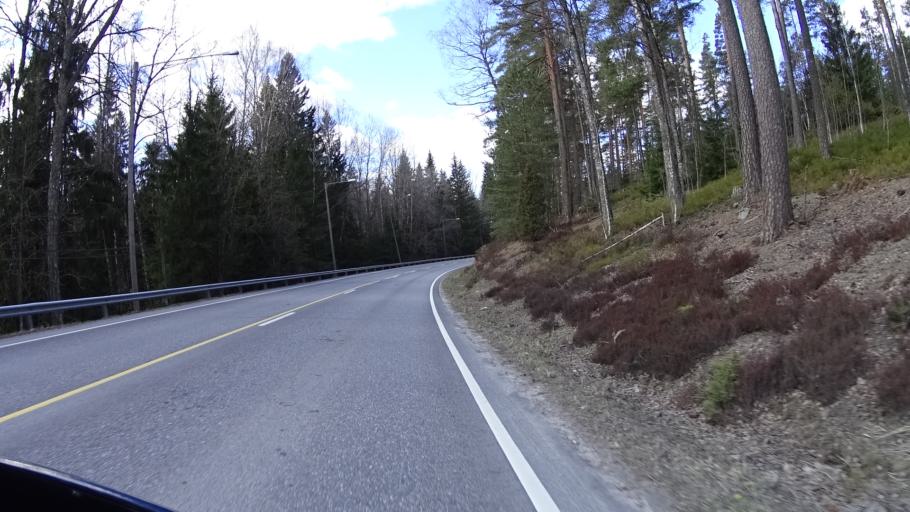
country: FI
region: Uusimaa
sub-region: Helsinki
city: Espoo
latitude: 60.2525
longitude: 24.5153
